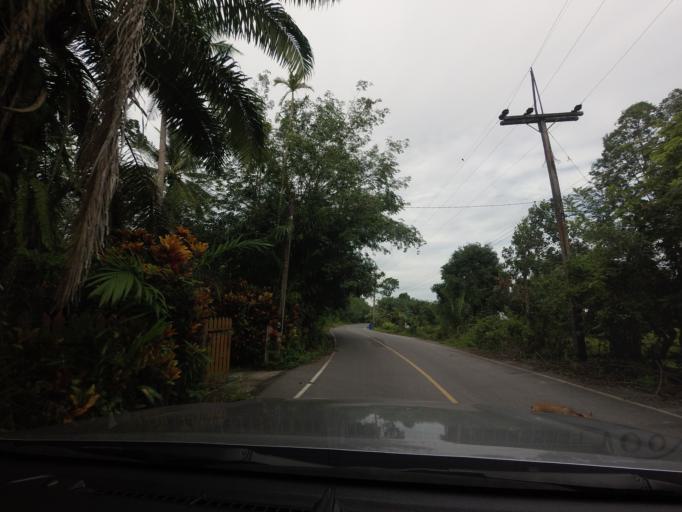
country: TH
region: Nakhon Si Thammarat
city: Phra Phrom
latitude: 8.2811
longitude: 99.9384
